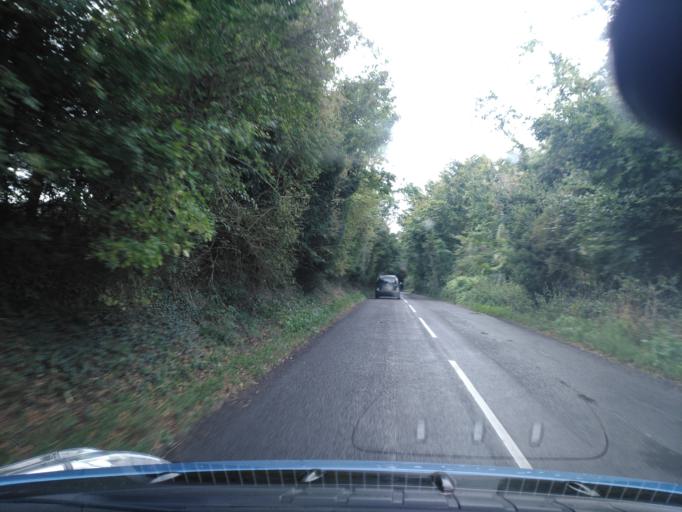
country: GB
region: England
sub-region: Oxfordshire
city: Stanford in the Vale
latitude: 51.5826
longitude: -1.5226
